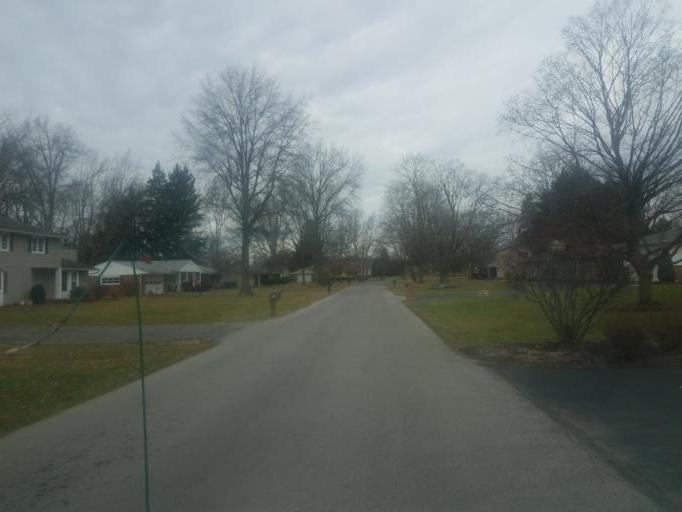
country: US
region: Ohio
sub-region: Marion County
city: Marion
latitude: 40.5691
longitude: -83.0827
